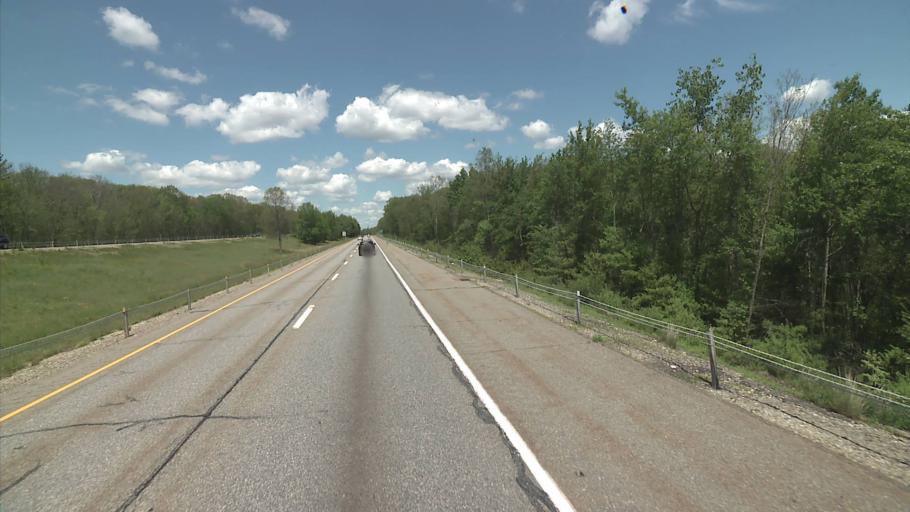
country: US
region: Connecticut
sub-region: Windham County
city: Thompson
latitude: 41.9940
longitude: -71.8526
